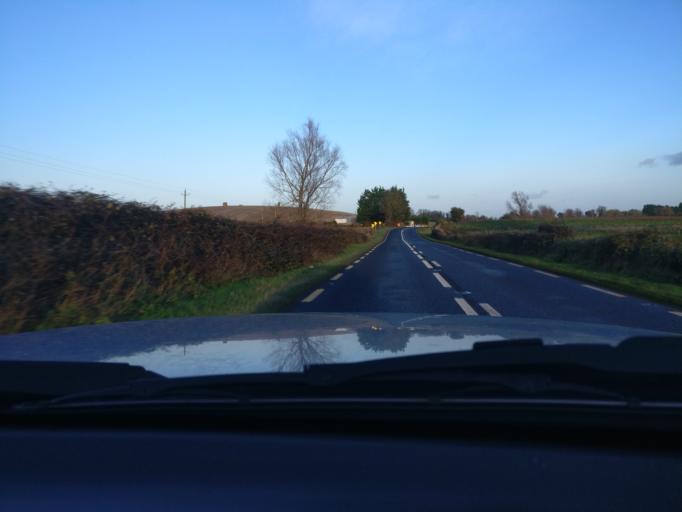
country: IE
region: Leinster
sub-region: Lu
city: Ardee
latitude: 53.8347
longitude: -6.6216
